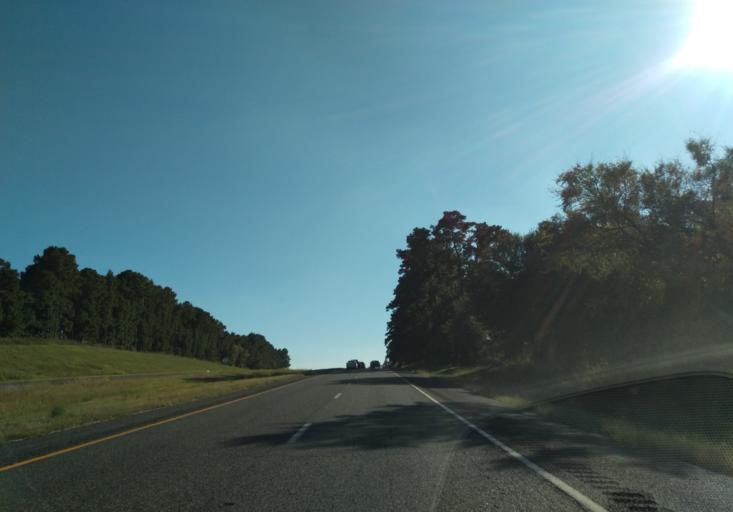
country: US
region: Texas
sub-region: Waller County
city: Hempstead
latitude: 30.2171
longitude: -96.0574
